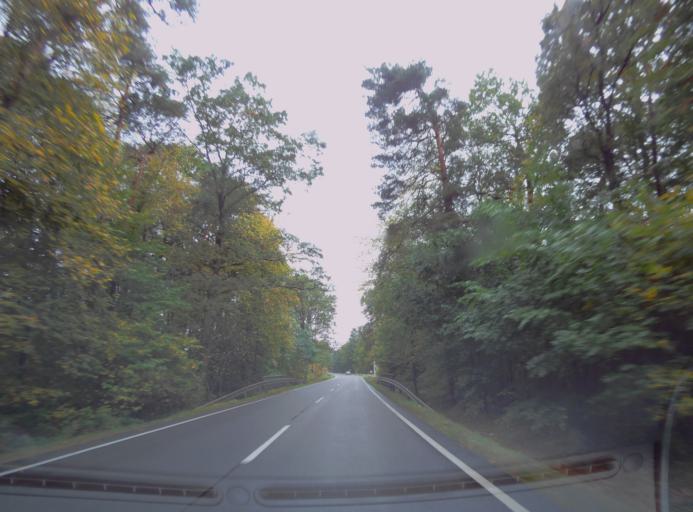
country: PL
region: Subcarpathian Voivodeship
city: Nowa Sarzyna
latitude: 50.2943
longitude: 22.3749
